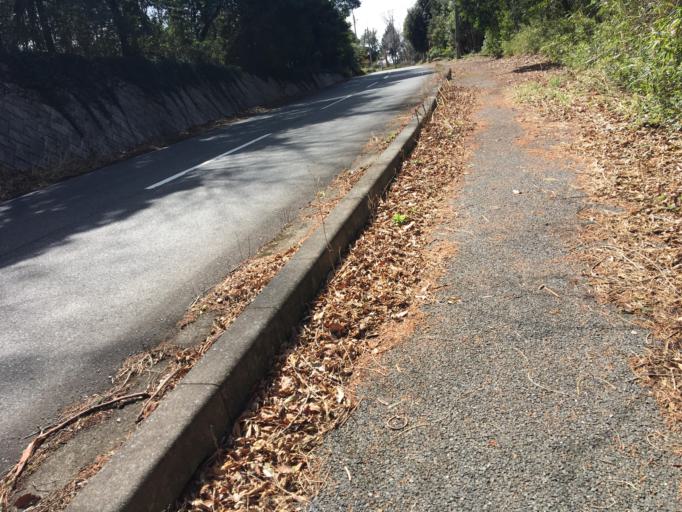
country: JP
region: Saitama
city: Ogawa
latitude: 36.0236
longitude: 139.3294
